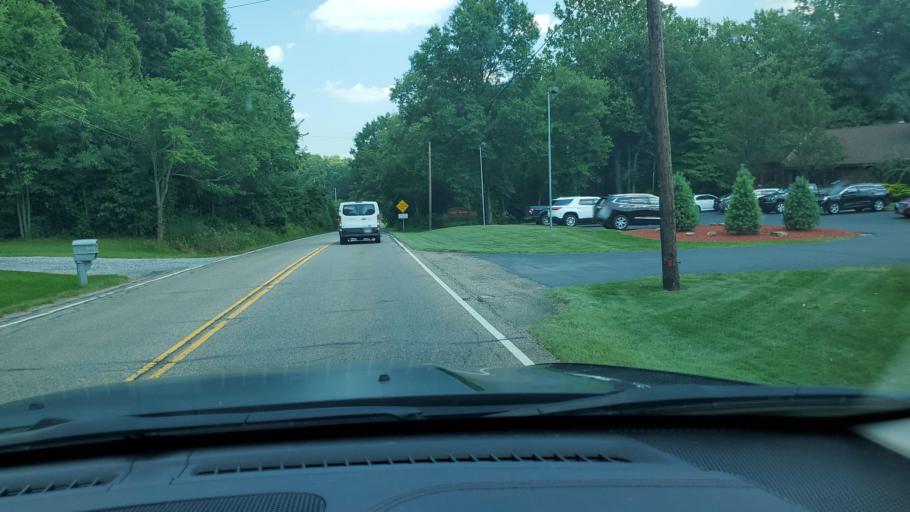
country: US
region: Ohio
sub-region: Trumbull County
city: McKinley Heights
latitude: 41.1824
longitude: -80.7086
